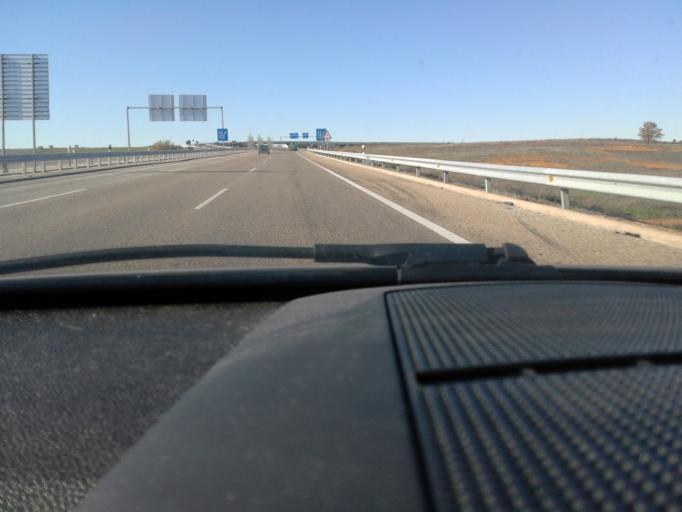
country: ES
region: Castille and Leon
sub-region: Provincia de Leon
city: Onzonilla
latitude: 42.5048
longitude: -5.5903
